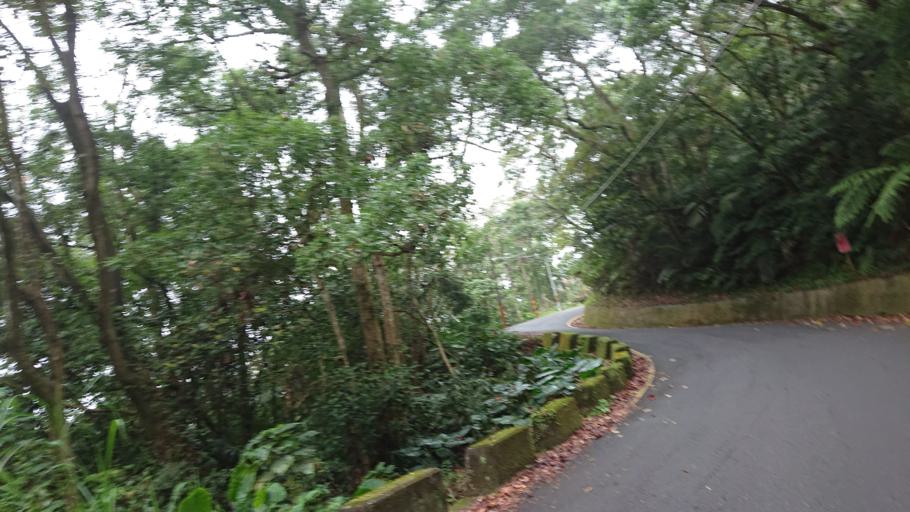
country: TW
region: Taiwan
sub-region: Taoyuan
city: Taoyuan
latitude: 24.9319
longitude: 121.3608
